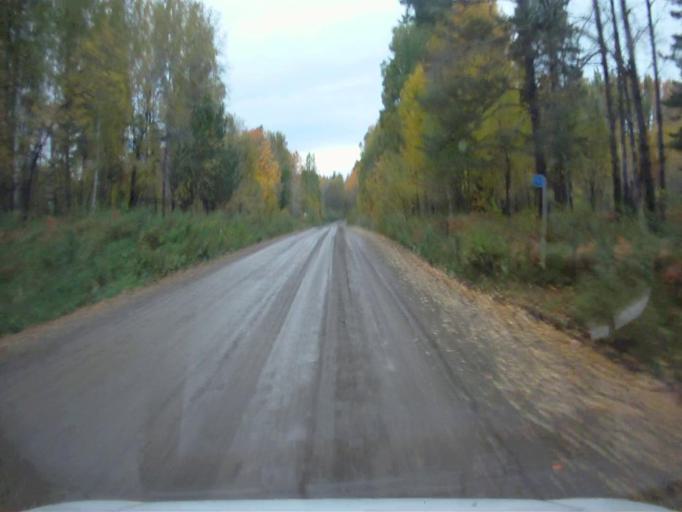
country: RU
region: Chelyabinsk
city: Nyazepetrovsk
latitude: 56.1122
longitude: 59.3701
